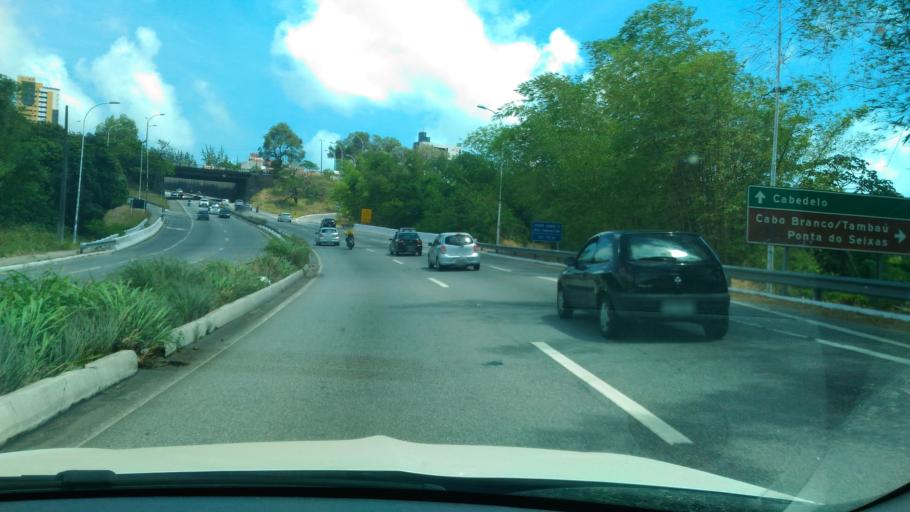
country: BR
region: Paraiba
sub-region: Joao Pessoa
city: Joao Pessoa
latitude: -7.1272
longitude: -34.8457
